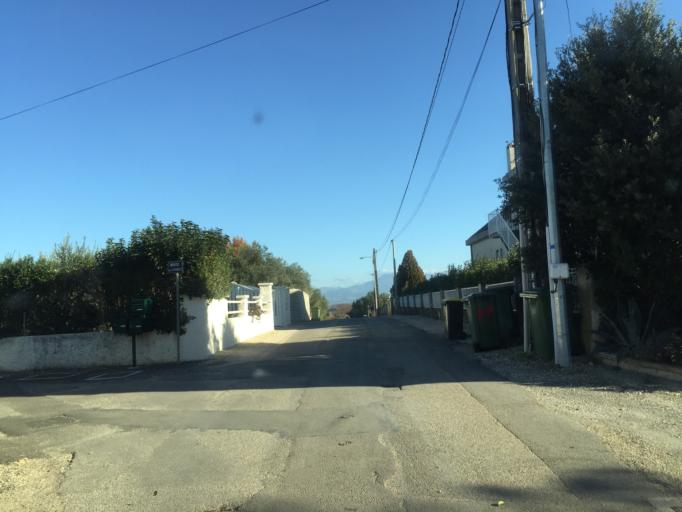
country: FR
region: Provence-Alpes-Cote d'Azur
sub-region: Departement du Vaucluse
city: Bedarrides
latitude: 44.0363
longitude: 4.8969
